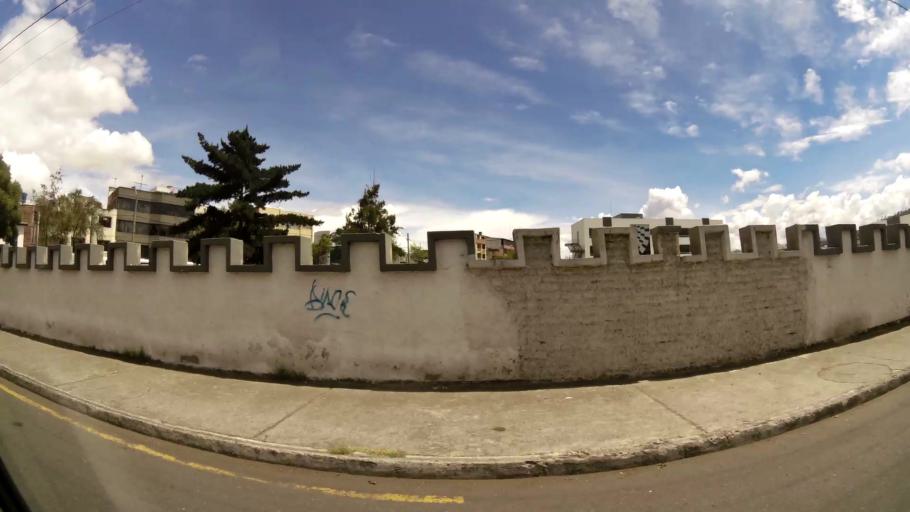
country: EC
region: Tungurahua
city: Ambato
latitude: -1.2526
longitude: -78.6332
